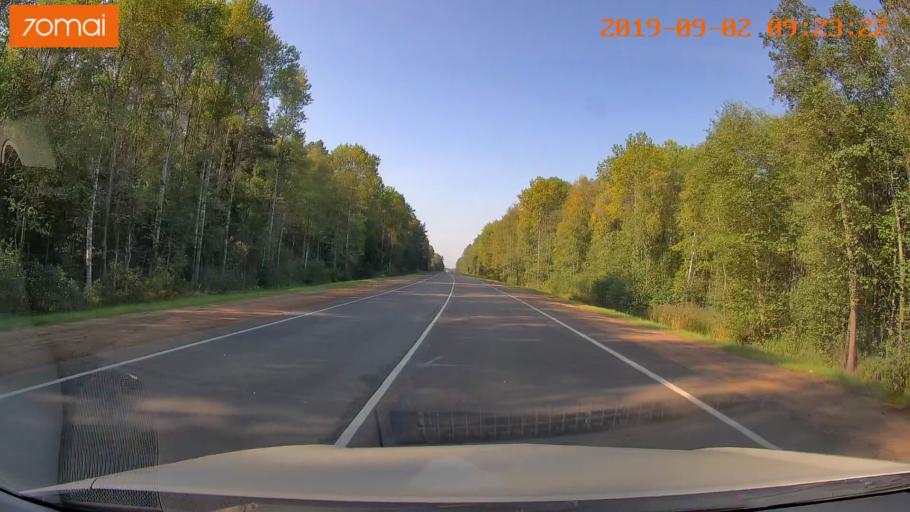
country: RU
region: Kaluga
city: Yukhnov
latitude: 54.7767
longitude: 35.3164
